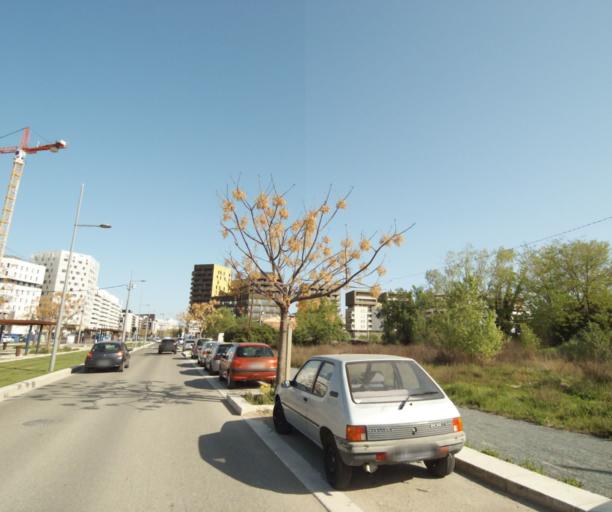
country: FR
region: Languedoc-Roussillon
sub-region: Departement de l'Herault
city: Lattes
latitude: 43.5970
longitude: 3.9043
